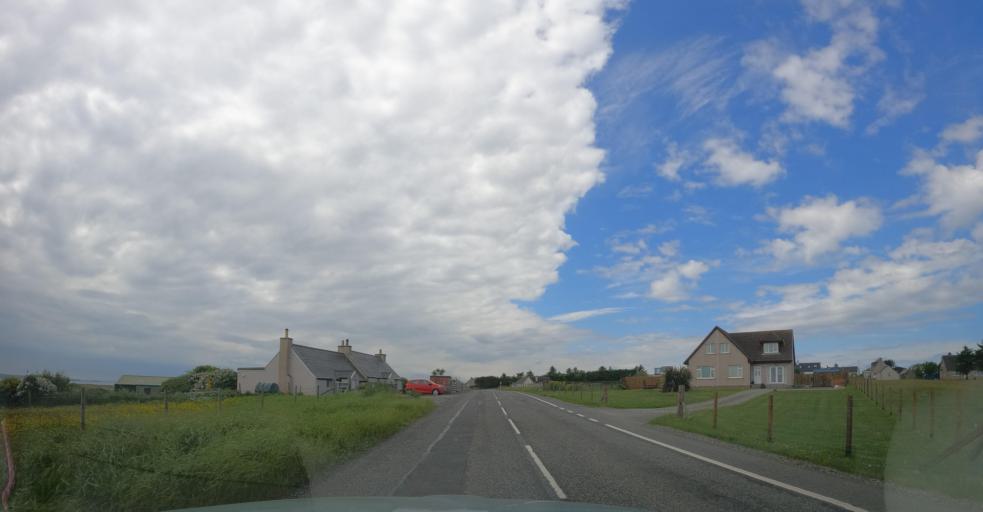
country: GB
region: Scotland
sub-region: Eilean Siar
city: Isle of Lewis
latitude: 58.2785
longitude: -6.2888
